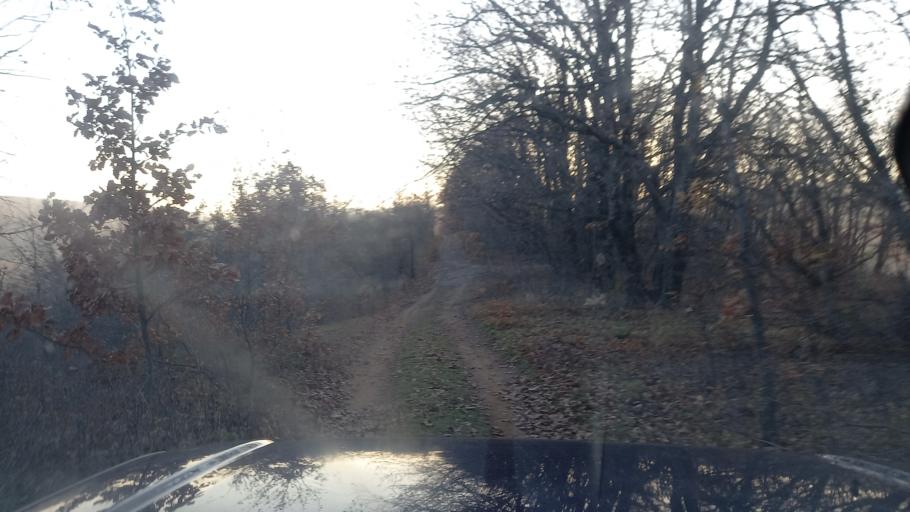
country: RU
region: Krasnodarskiy
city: Azovskaya
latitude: 44.8132
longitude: 38.6048
